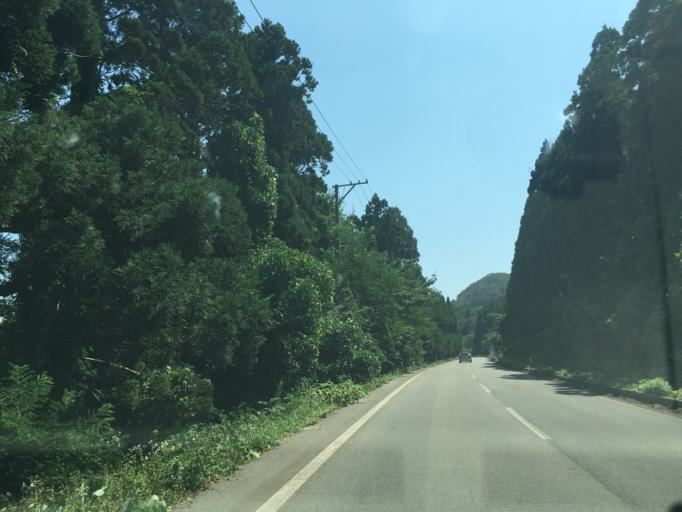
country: JP
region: Akita
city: Tenno
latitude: 39.9917
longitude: 139.7130
